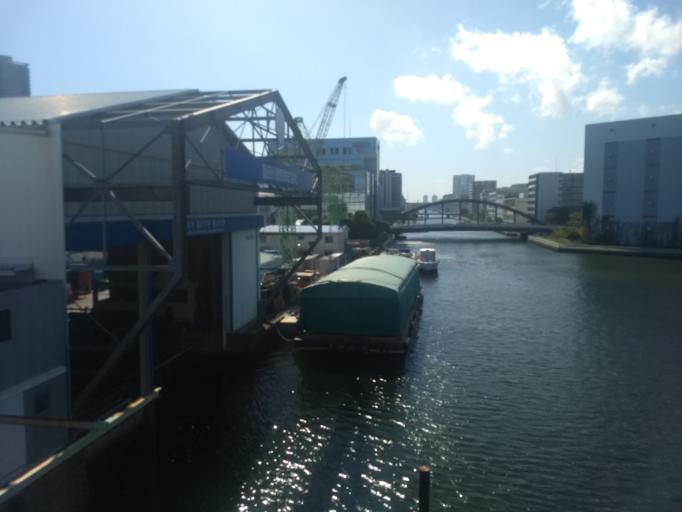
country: JP
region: Tokyo
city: Urayasu
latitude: 35.6604
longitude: 139.8156
